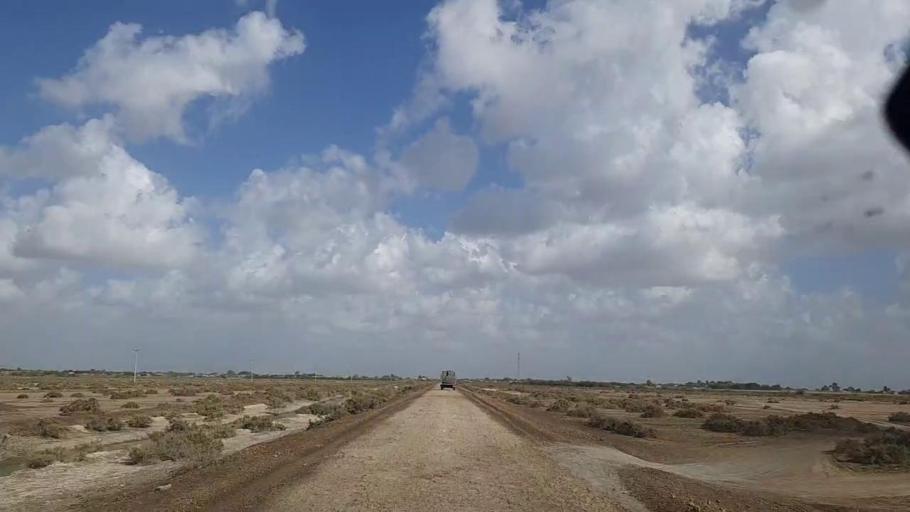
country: PK
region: Sindh
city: Keti Bandar
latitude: 24.1058
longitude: 67.5897
